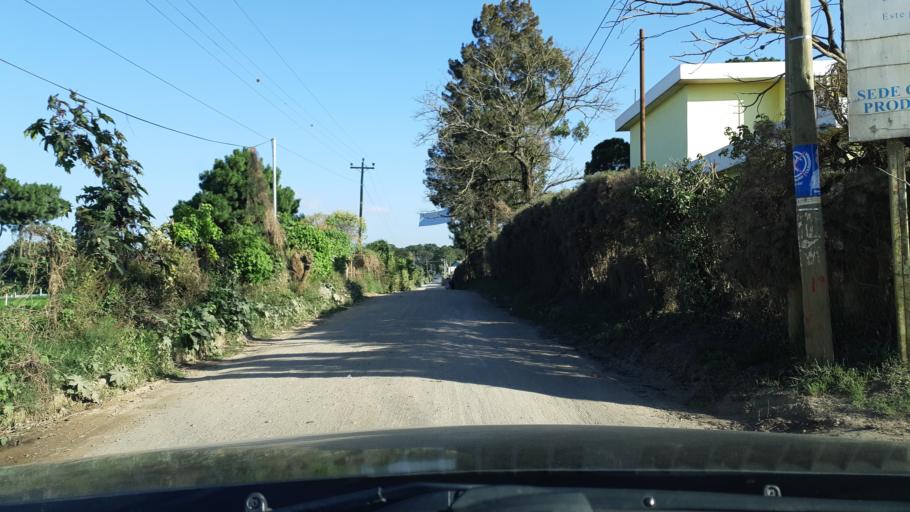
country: GT
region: Chimaltenango
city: El Tejar
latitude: 14.6384
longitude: -90.8037
